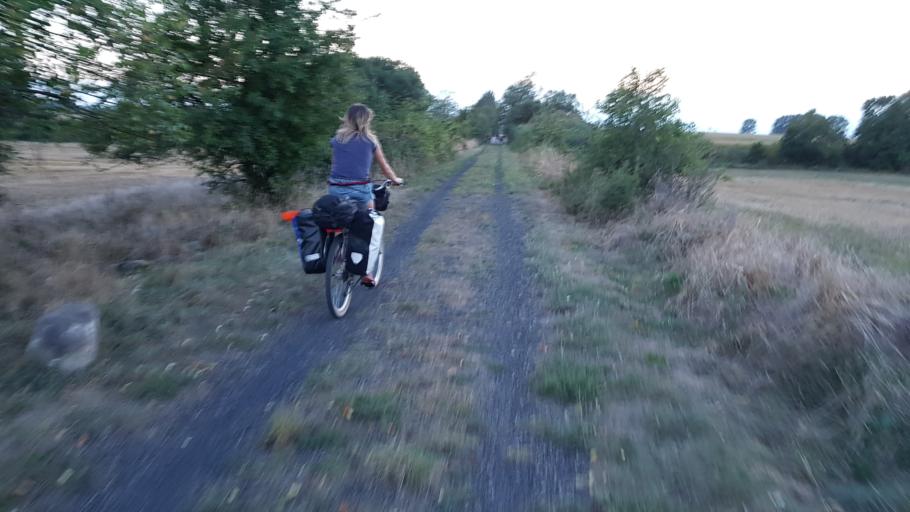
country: PL
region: West Pomeranian Voivodeship
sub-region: Powiat pyrzycki
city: Przelewice
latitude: 53.1311
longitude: 15.0356
